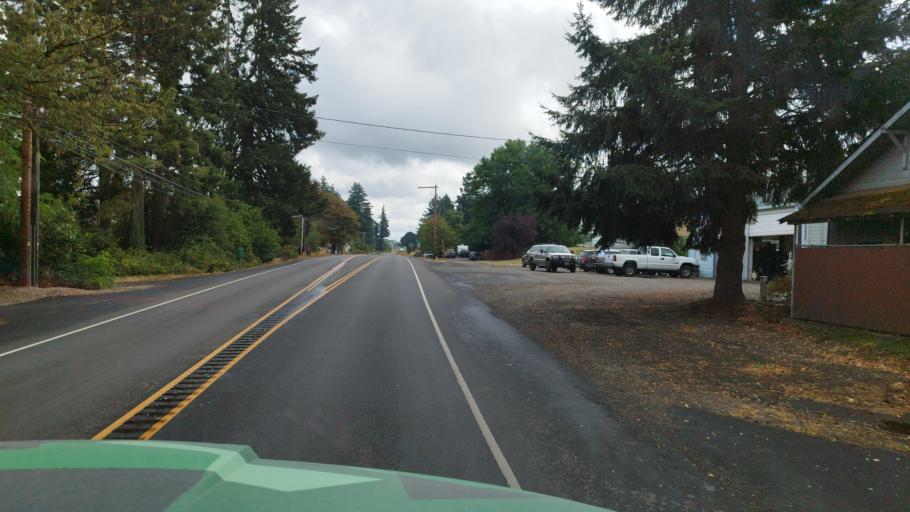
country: US
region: Oregon
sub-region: Yamhill County
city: Lafayette
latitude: 45.2426
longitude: -123.1068
